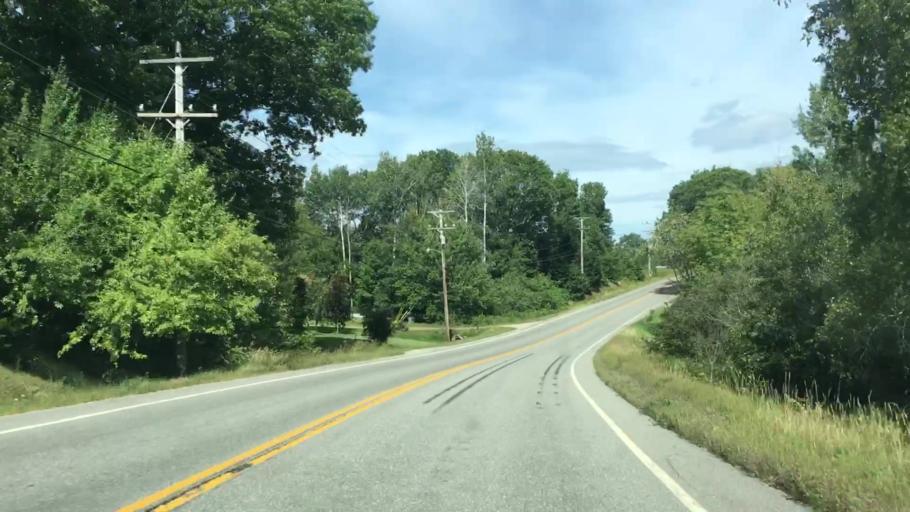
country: US
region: Maine
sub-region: Penobscot County
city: Lincoln
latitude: 45.4202
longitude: -68.4896
